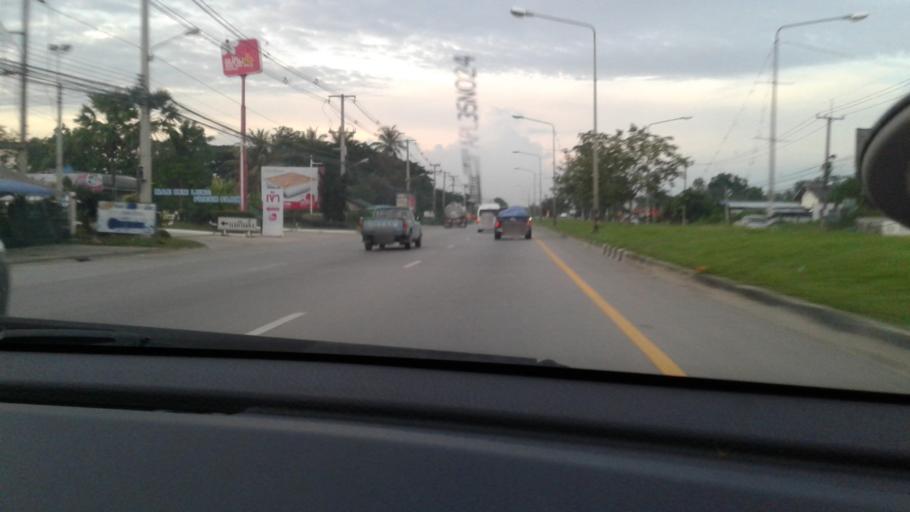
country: TH
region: Phetchaburi
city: Cha-am
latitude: 12.8432
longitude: 99.9293
